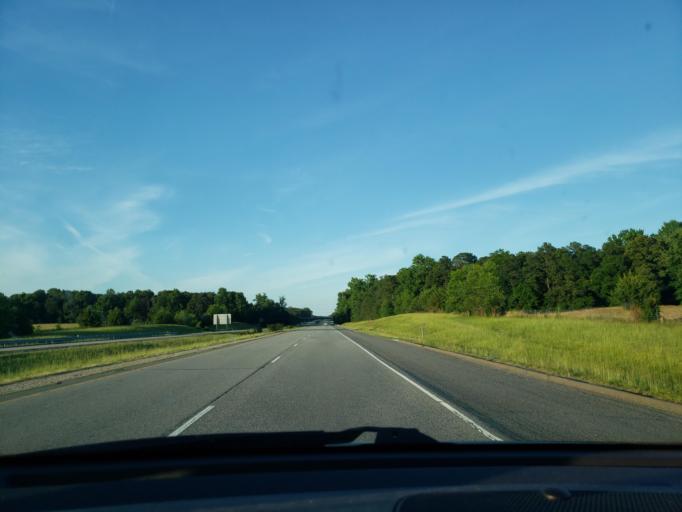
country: US
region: Virginia
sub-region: Henrico County
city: Fort Lee
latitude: 37.4671
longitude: -77.3696
